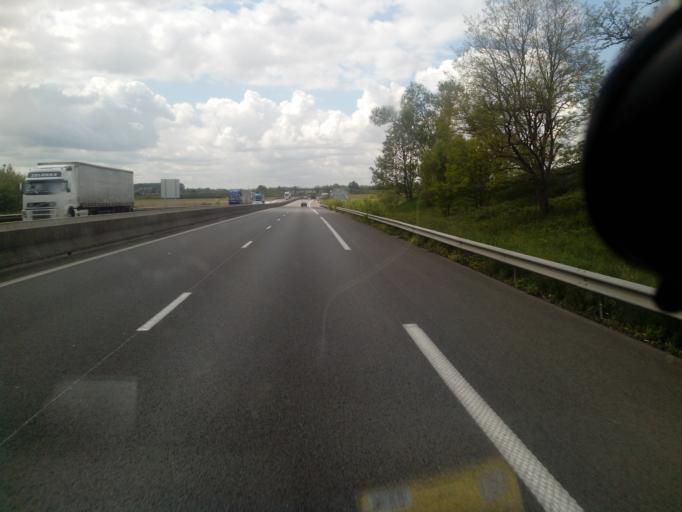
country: FR
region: Nord-Pas-de-Calais
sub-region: Departement du Nord
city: Meteren
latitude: 50.7521
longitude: 2.6610
